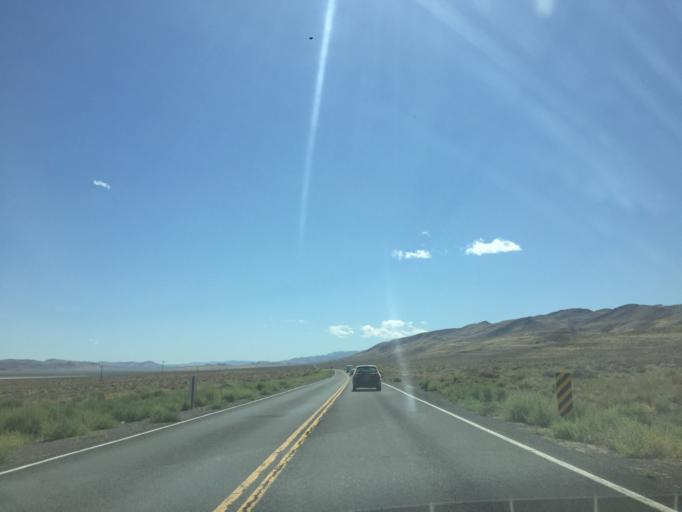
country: US
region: Nevada
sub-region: Lyon County
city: Fernley
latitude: 40.0461
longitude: -119.3844
